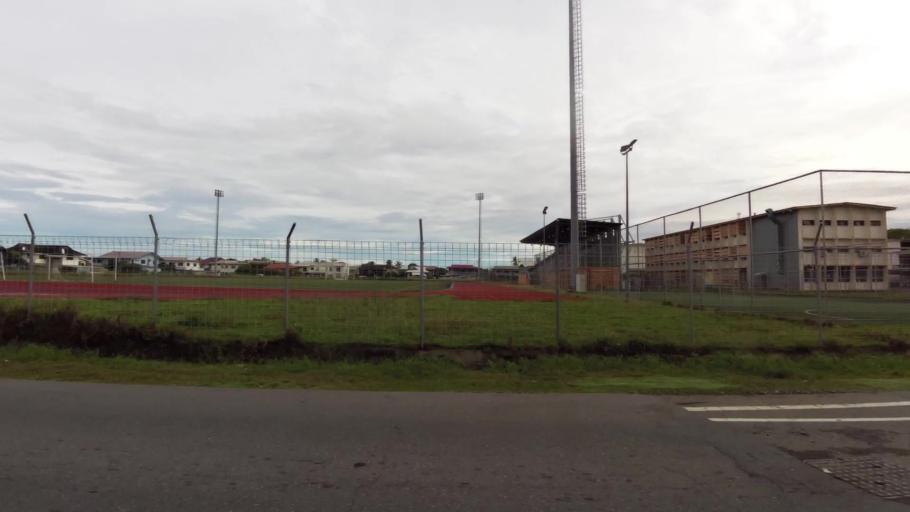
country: BN
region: Belait
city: Seria
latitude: 4.6080
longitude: 114.3308
